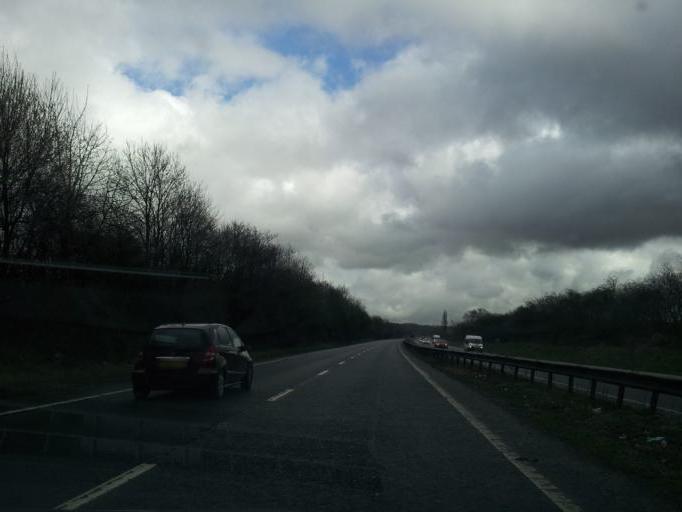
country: GB
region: England
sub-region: Somerset
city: Castle Cary
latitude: 51.0373
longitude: -2.5536
